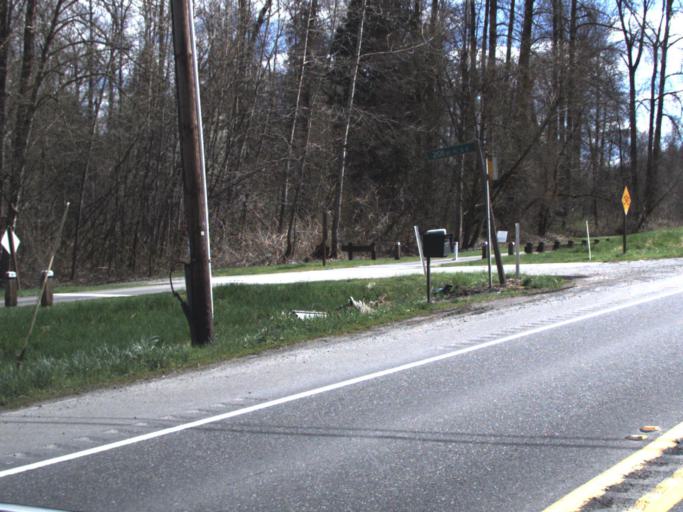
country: US
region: Washington
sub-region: King County
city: Maple Heights-Lake Desire
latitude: 47.4442
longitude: -122.0731
